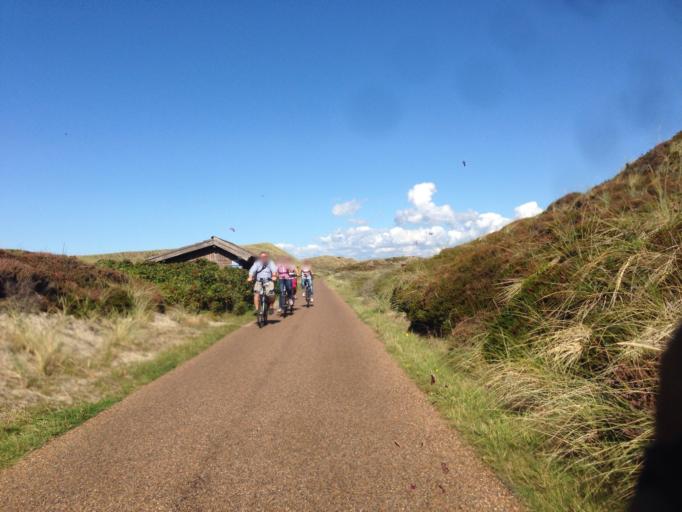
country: DE
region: Schleswig-Holstein
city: List
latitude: 55.0003
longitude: 8.3649
